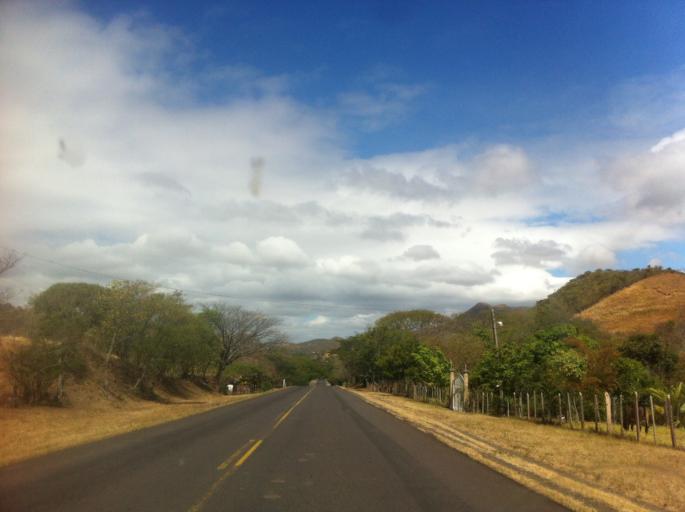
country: NI
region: Chontales
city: Acoyapa
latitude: 12.0220
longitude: -85.2552
